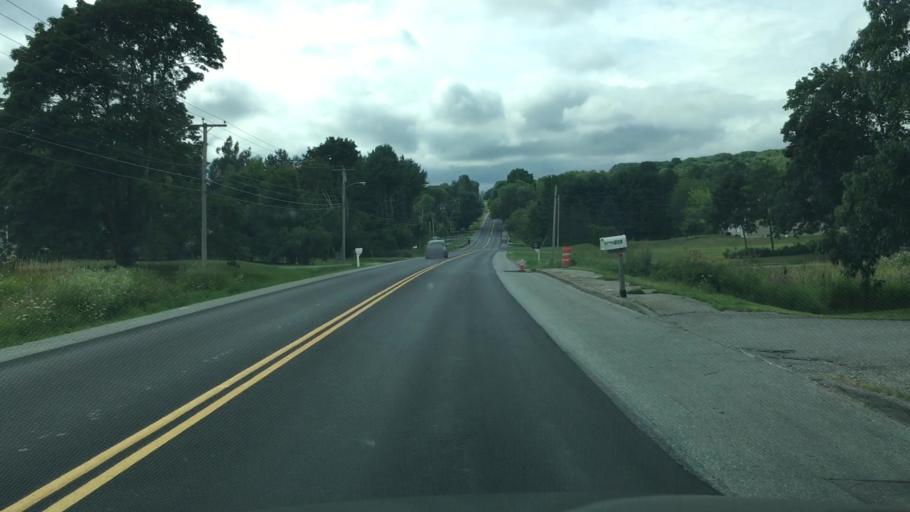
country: US
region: Maine
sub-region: Penobscot County
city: Hampden
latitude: 44.7461
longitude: -68.8584
